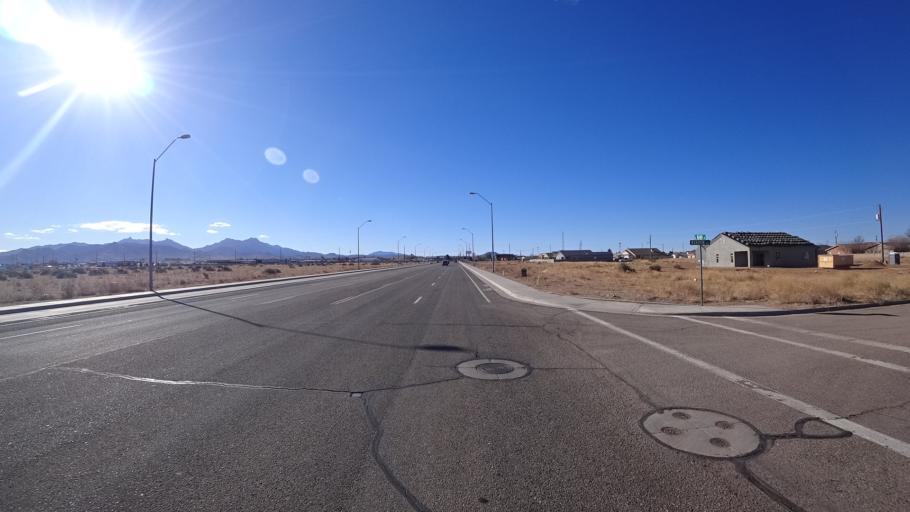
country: US
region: Arizona
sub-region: Mohave County
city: New Kingman-Butler
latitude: 35.2284
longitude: -114.0116
